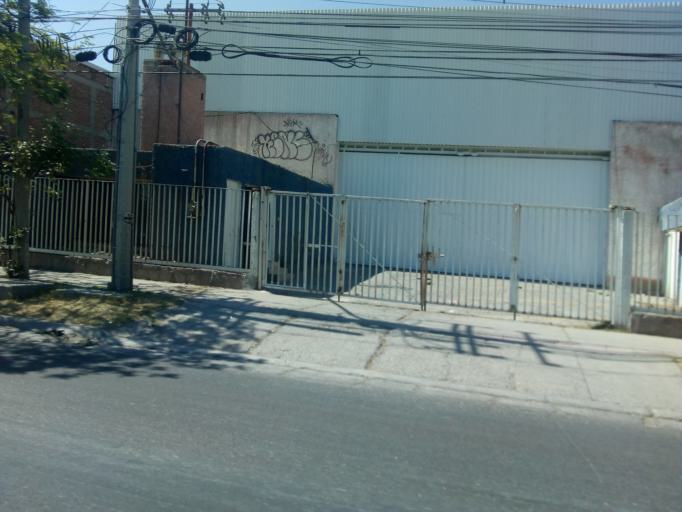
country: MX
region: Guanajuato
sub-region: Leon
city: Centro Familiar la Soledad
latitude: 21.0997
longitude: -101.7200
